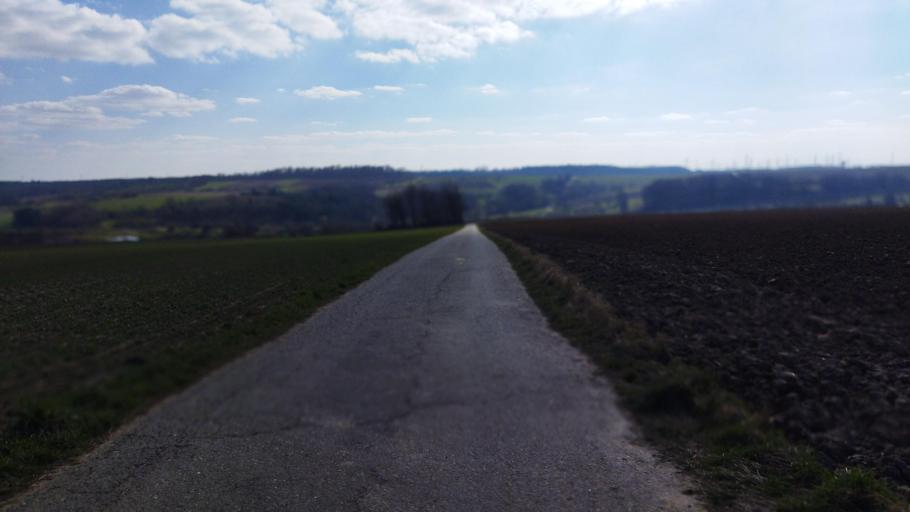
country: DE
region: Baden-Wuerttemberg
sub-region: Regierungsbezirk Stuttgart
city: Ilsfeld
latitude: 49.0606
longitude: 9.2250
